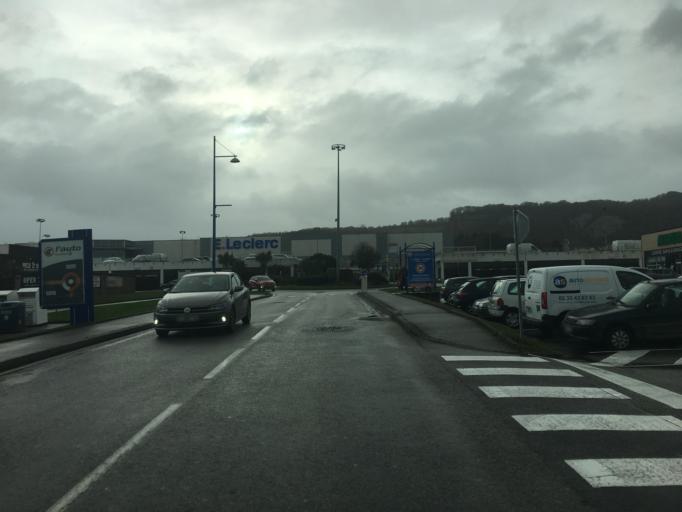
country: FR
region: Lower Normandy
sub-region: Departement de la Manche
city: Cherbourg-Octeville
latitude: 49.6336
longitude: -1.5921
